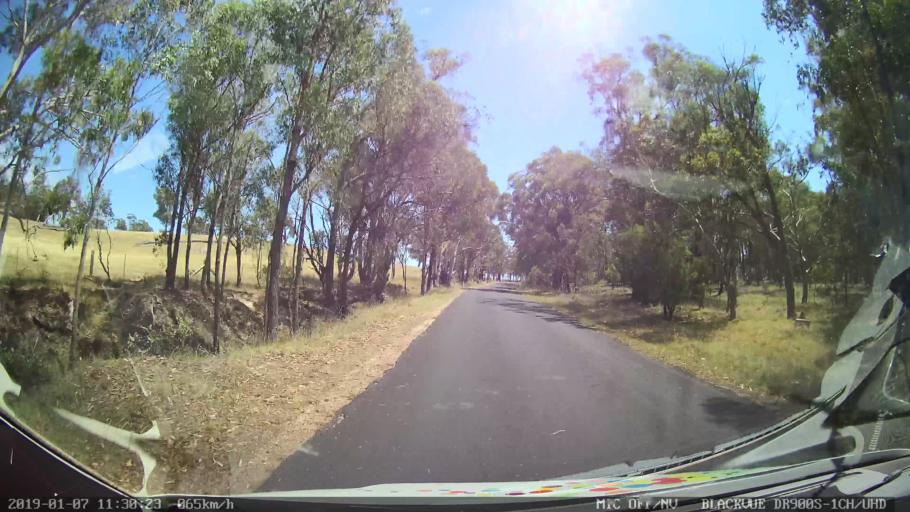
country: AU
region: New South Wales
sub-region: Armidale Dumaresq
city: Armidale
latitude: -30.4297
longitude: 151.5635
